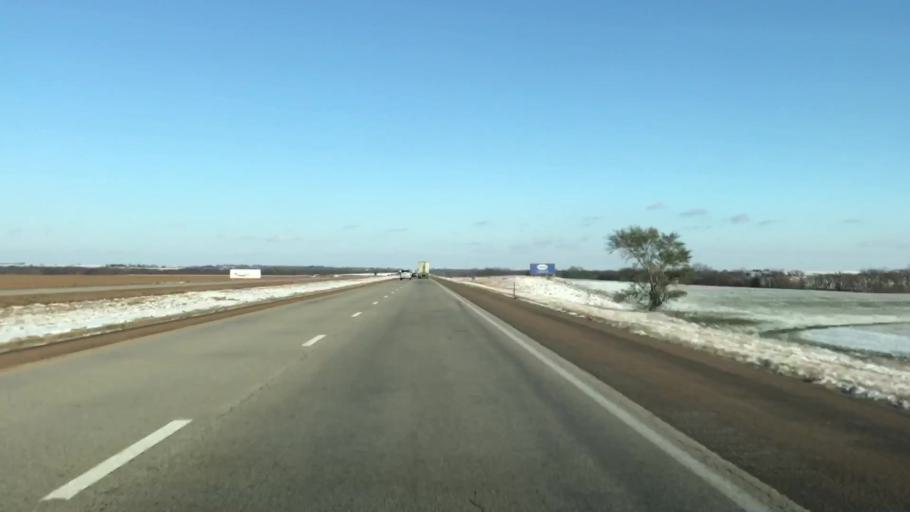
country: US
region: Kansas
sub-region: Saline County
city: Salina
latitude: 38.8782
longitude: -97.8245
